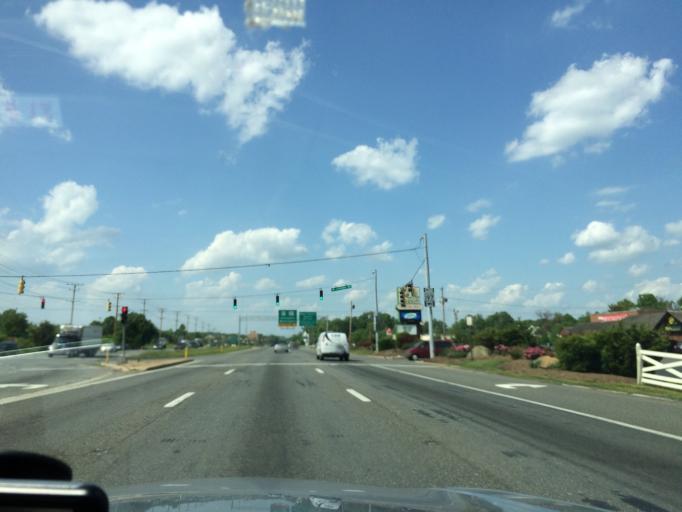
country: US
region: Maryland
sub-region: Prince George's County
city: Bowie
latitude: 38.9418
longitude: -76.7179
